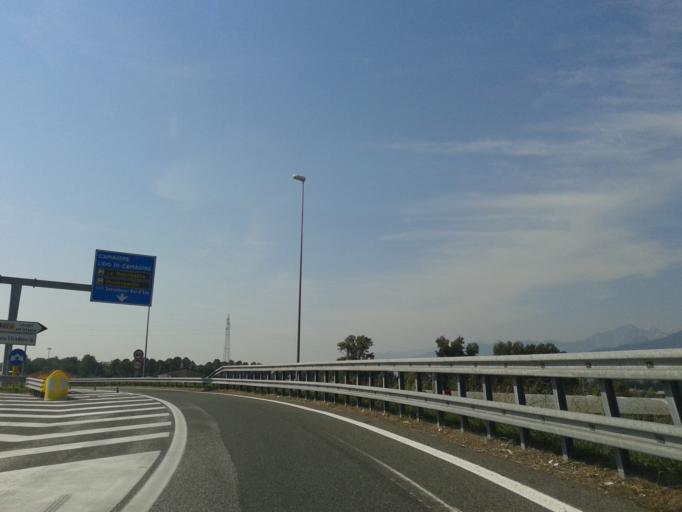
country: IT
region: Tuscany
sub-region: Provincia di Lucca
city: Camaiore
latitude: 43.8967
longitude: 10.2582
